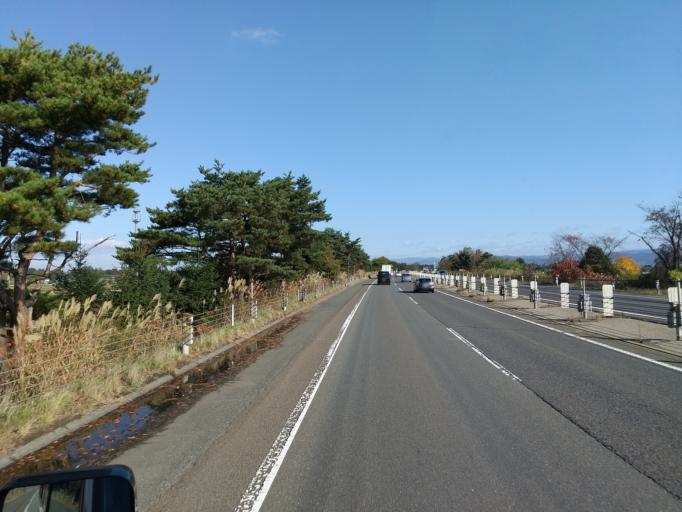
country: JP
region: Iwate
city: Morioka-shi
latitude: 39.5992
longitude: 141.1199
